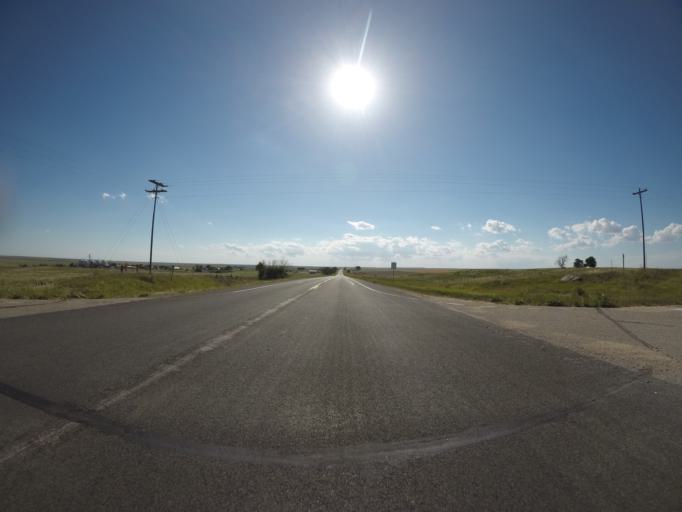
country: US
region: Colorado
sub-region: Morgan County
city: Brush
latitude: 40.6101
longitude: -103.6575
